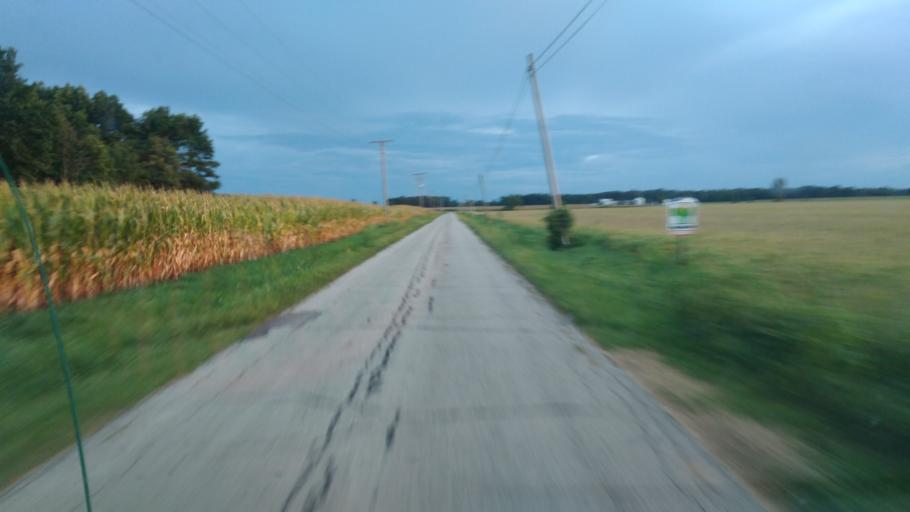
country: US
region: Ohio
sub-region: Crawford County
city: Bucyrus
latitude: 40.7100
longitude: -82.9189
